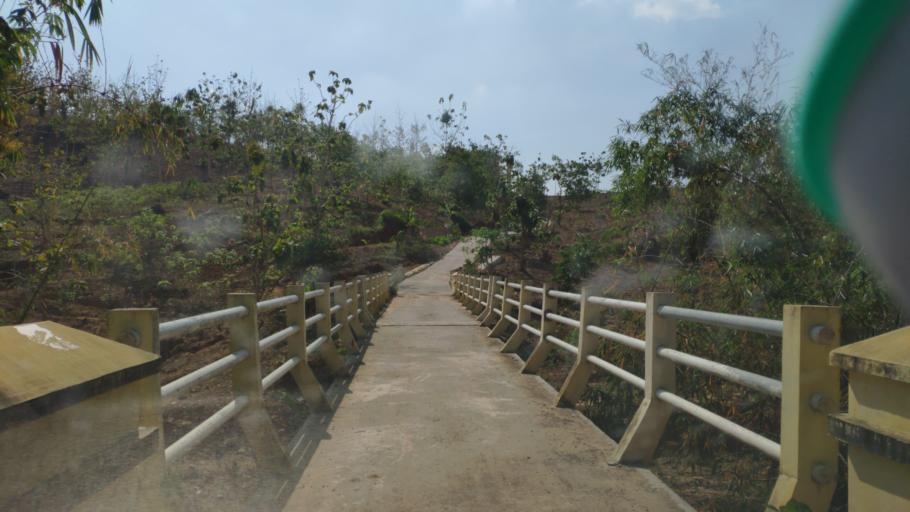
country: ID
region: Central Java
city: Ngapus
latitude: -6.9311
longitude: 111.2175
